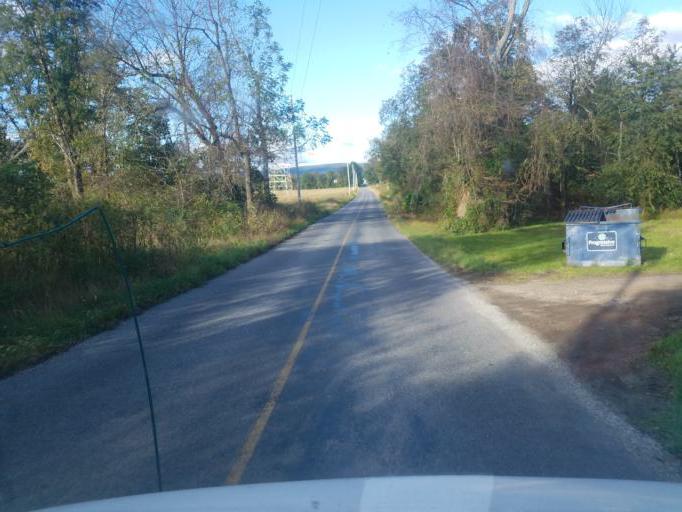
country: US
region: Pennsylvania
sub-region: Adams County
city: Biglerville
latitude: 39.8837
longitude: -77.3163
